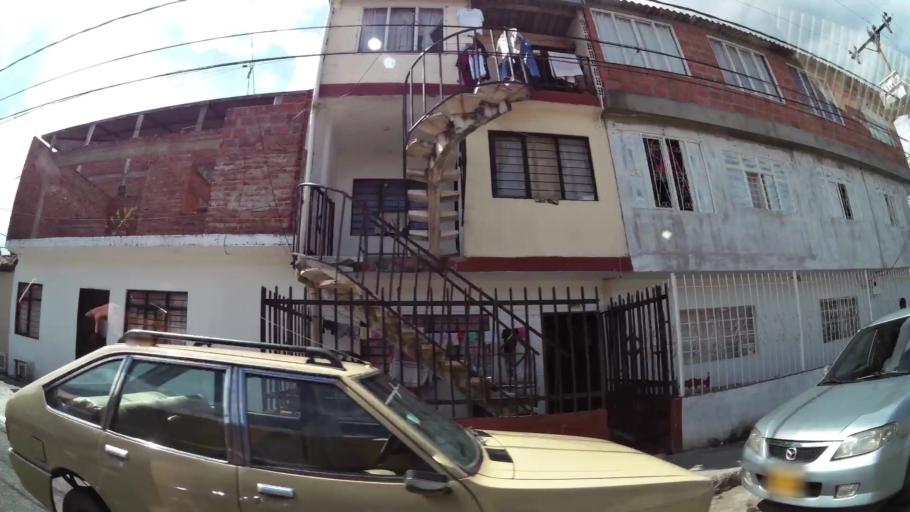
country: CO
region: Valle del Cauca
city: Cali
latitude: 3.4030
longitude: -76.5136
